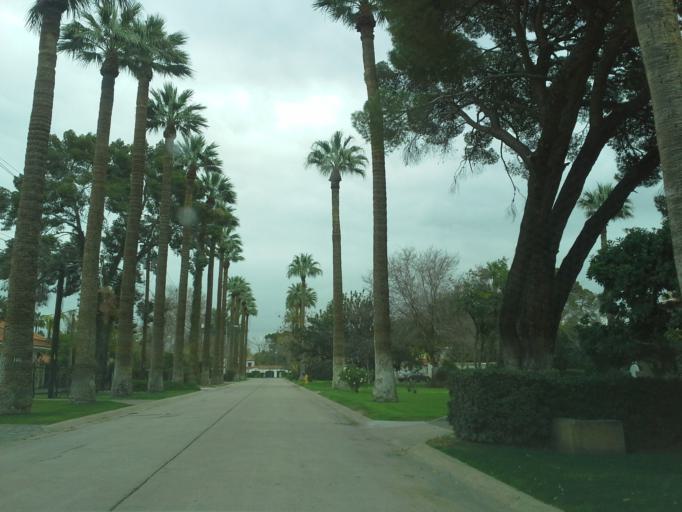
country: US
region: Arizona
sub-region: Maricopa County
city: Phoenix
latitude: 33.4809
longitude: -112.0596
